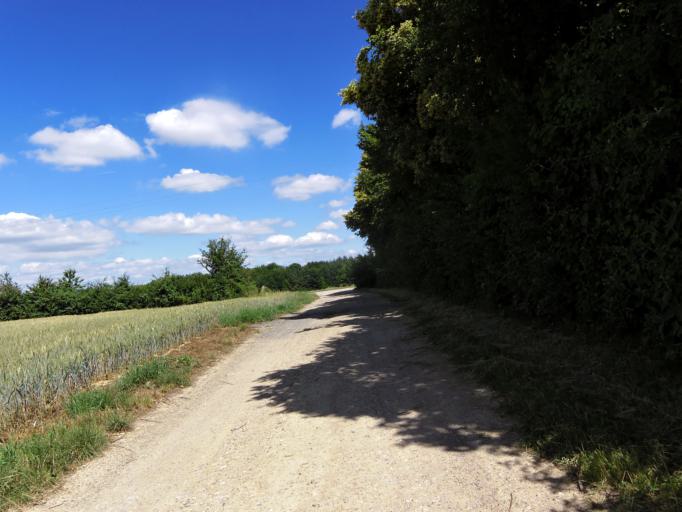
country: DE
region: Bavaria
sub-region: Regierungsbezirk Unterfranken
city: Kist
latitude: 49.7510
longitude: 9.8434
